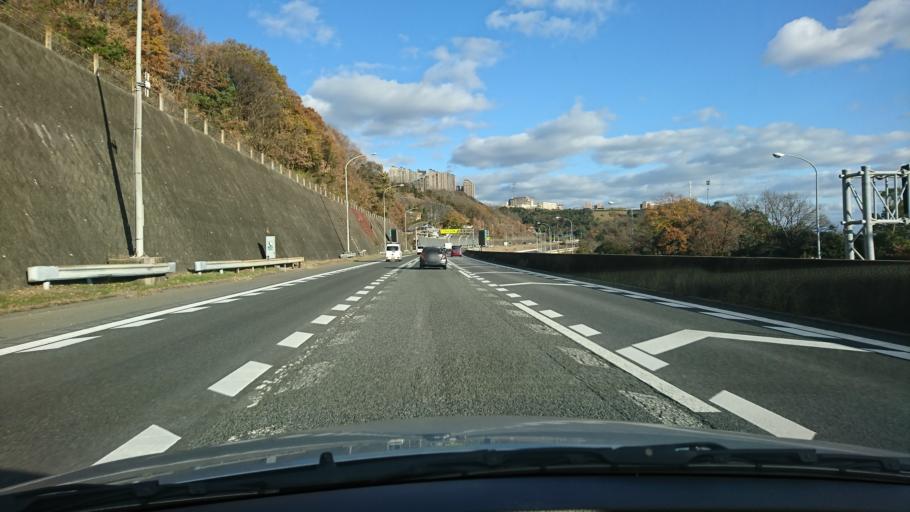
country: JP
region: Hyogo
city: Takarazuka
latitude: 34.8223
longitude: 135.3265
